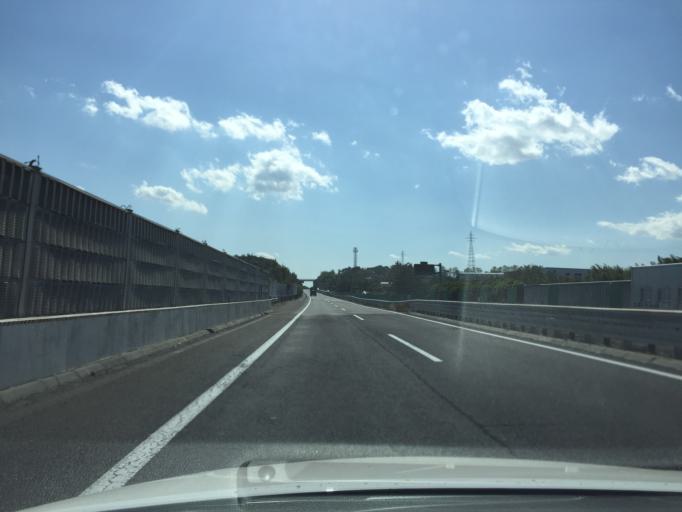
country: JP
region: Fukushima
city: Sukagawa
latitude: 37.2857
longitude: 140.3509
